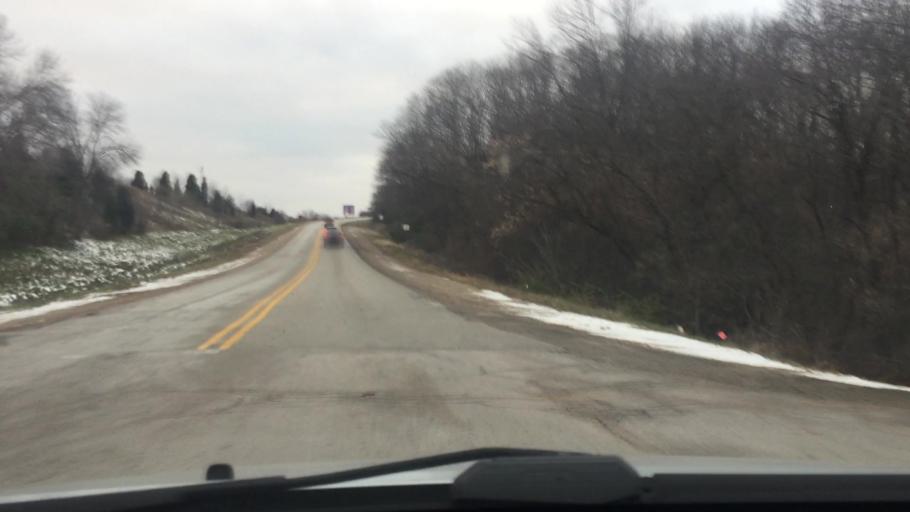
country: US
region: Wisconsin
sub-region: Waukesha County
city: Wales
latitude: 43.0498
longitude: -88.3495
